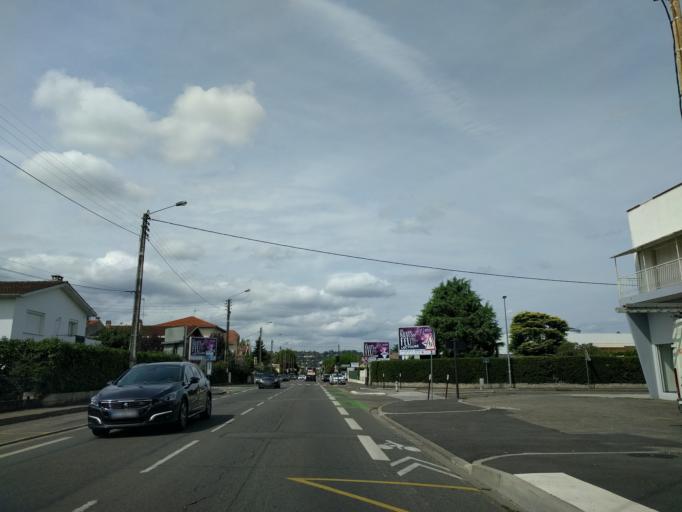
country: FR
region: Aquitaine
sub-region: Departement du Lot-et-Garonne
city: Agen
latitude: 44.1893
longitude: 0.6304
